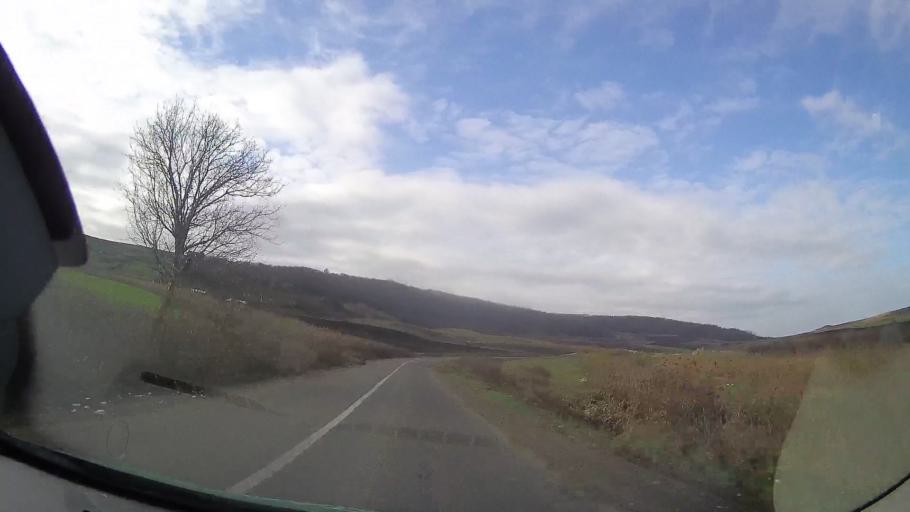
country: RO
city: Barza
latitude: 46.5533
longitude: 24.1094
